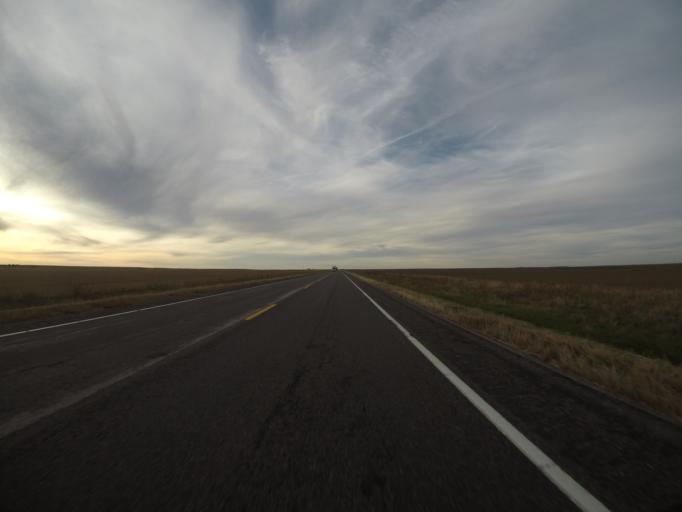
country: US
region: Colorado
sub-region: Yuma County
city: Yuma
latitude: 39.6932
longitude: -102.9834
